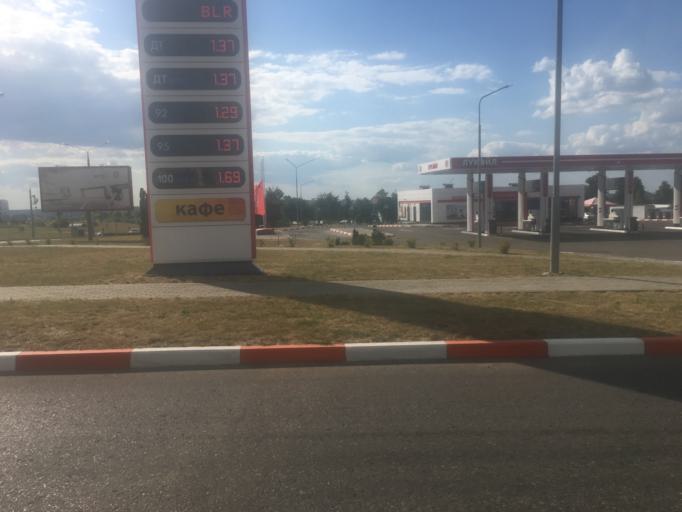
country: BY
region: Grodnenskaya
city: Hrodna
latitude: 53.6472
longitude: 23.8125
